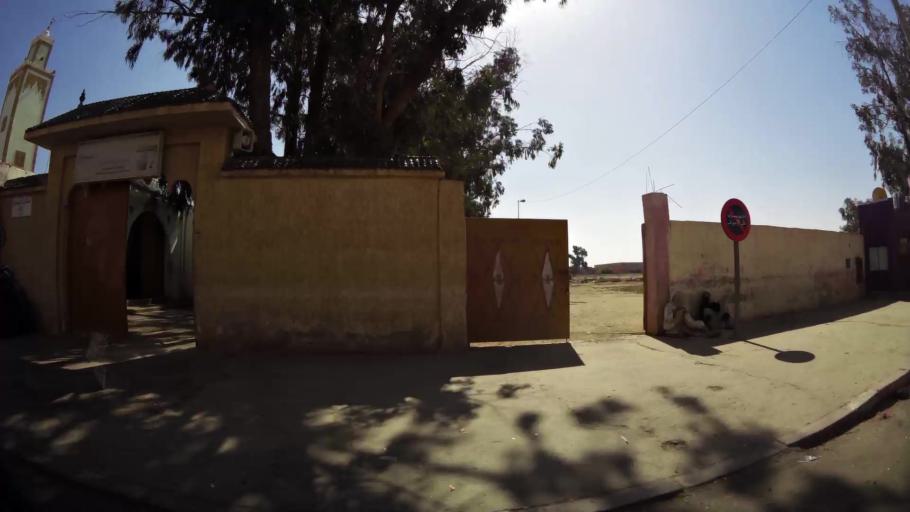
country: MA
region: Souss-Massa-Draa
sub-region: Inezgane-Ait Mellou
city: Inezgane
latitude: 30.3321
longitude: -9.5184
